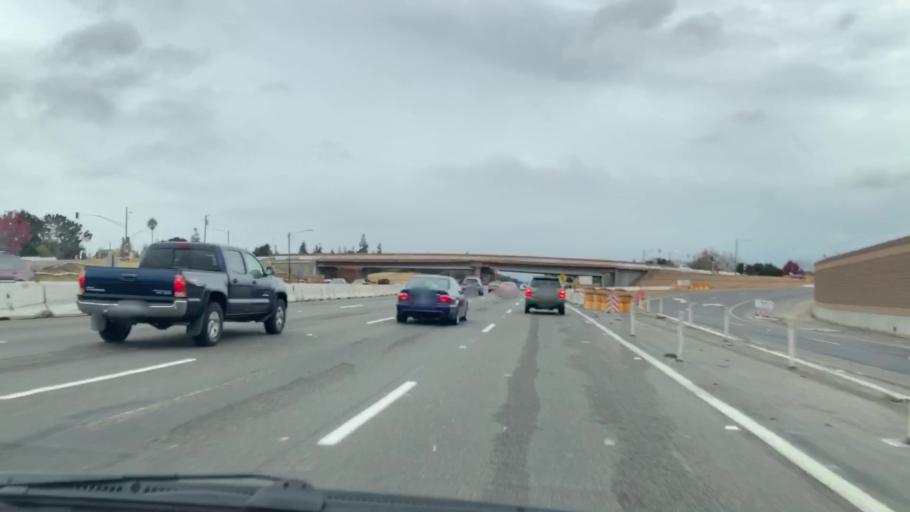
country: US
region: California
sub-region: San Mateo County
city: East Palo Alto
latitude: 37.4679
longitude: -122.1532
